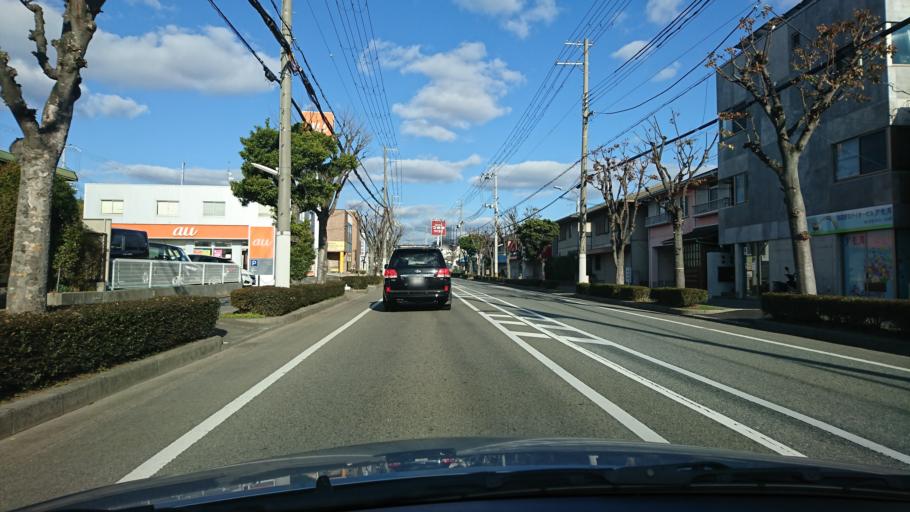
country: JP
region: Hyogo
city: Akashi
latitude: 34.6724
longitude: 135.0086
